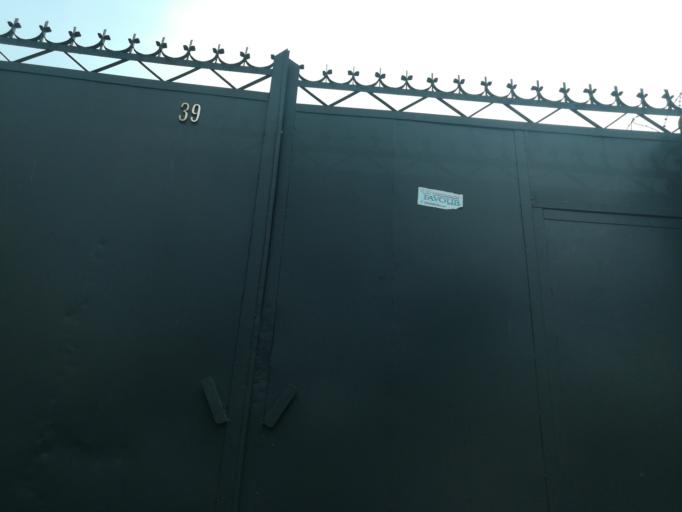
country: NG
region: Rivers
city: Port Harcourt
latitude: 4.8195
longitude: 7.0179
